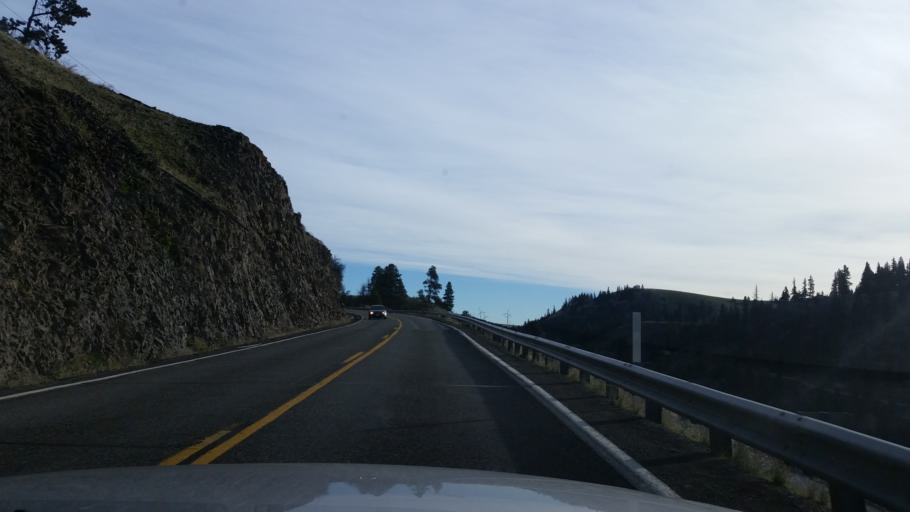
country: US
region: Washington
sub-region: Kittitas County
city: Cle Elum
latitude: 47.1305
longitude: -120.7740
